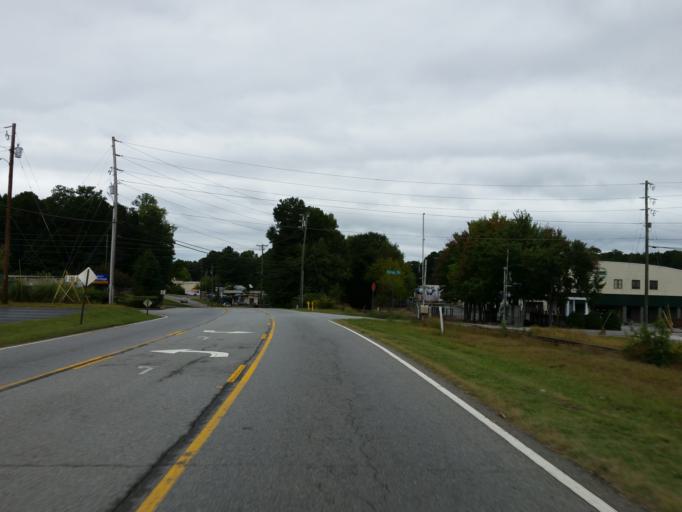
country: US
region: Georgia
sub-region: Cobb County
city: Marietta
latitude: 33.9981
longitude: -84.5238
